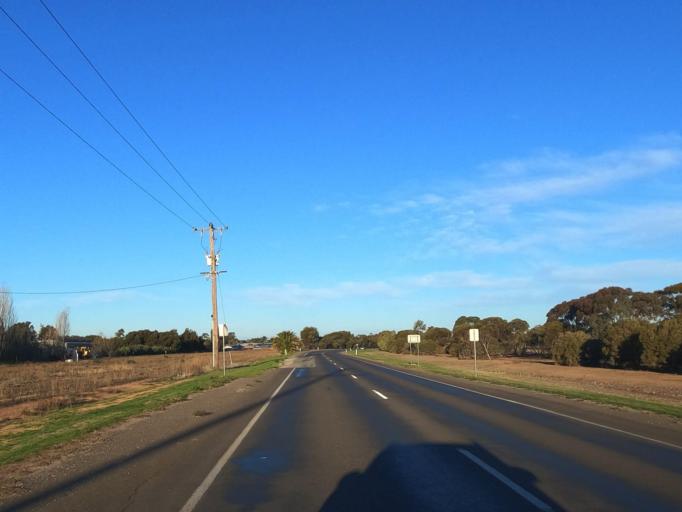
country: AU
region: Victoria
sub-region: Swan Hill
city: Swan Hill
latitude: -35.3367
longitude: 143.5359
